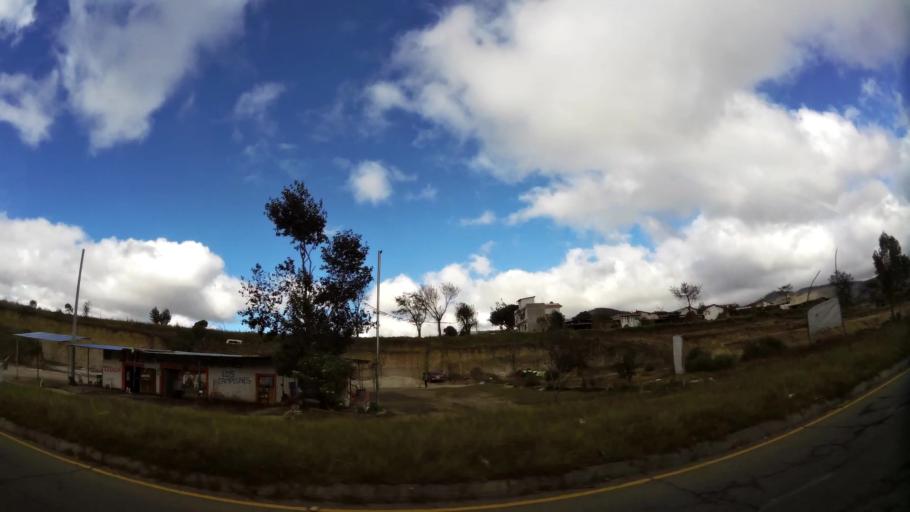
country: GT
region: Quetzaltenango
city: Salcaja
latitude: 14.8785
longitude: -91.4704
